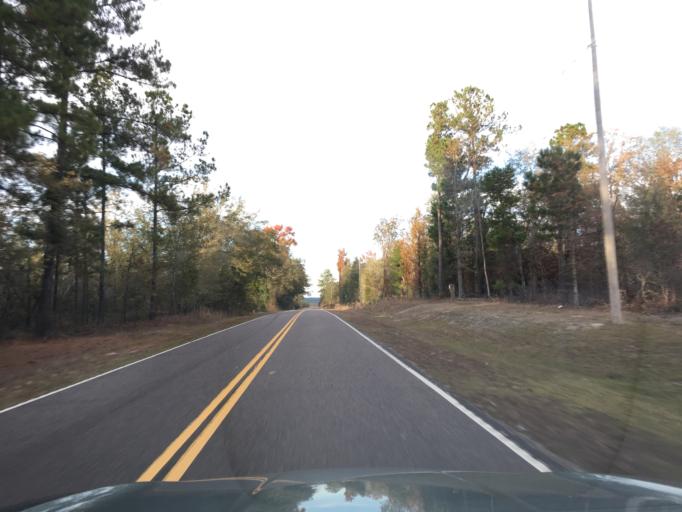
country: US
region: South Carolina
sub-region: Lexington County
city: Red Bank
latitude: 33.7074
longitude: -81.3560
